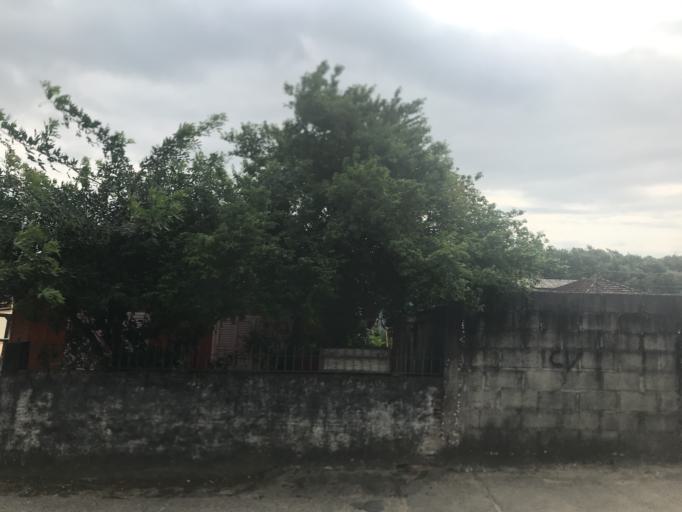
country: BR
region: Santa Catarina
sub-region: Florianopolis
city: Costeira do Pirajubae
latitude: -27.6444
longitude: -48.5219
